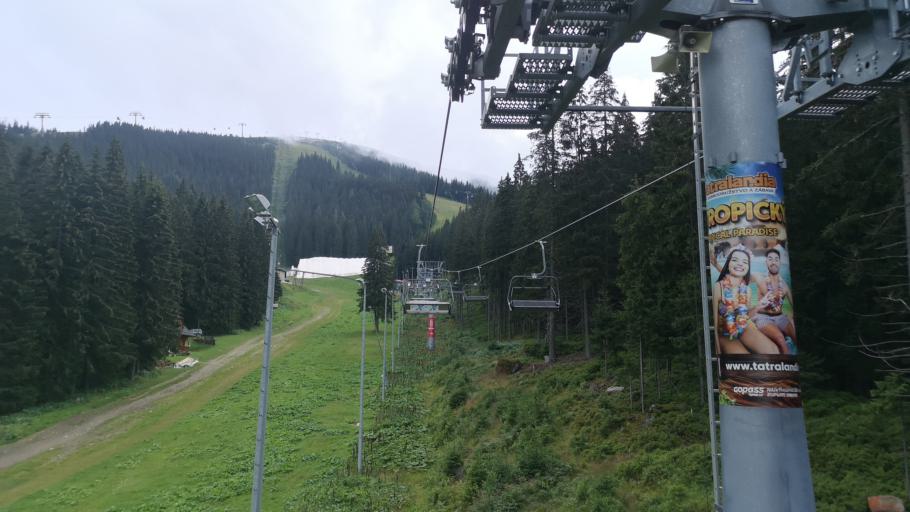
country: SK
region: Zilinsky
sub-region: Okres Liptovsky Mikulas
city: Liptovsky Mikulas
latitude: 48.9660
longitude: 19.5842
